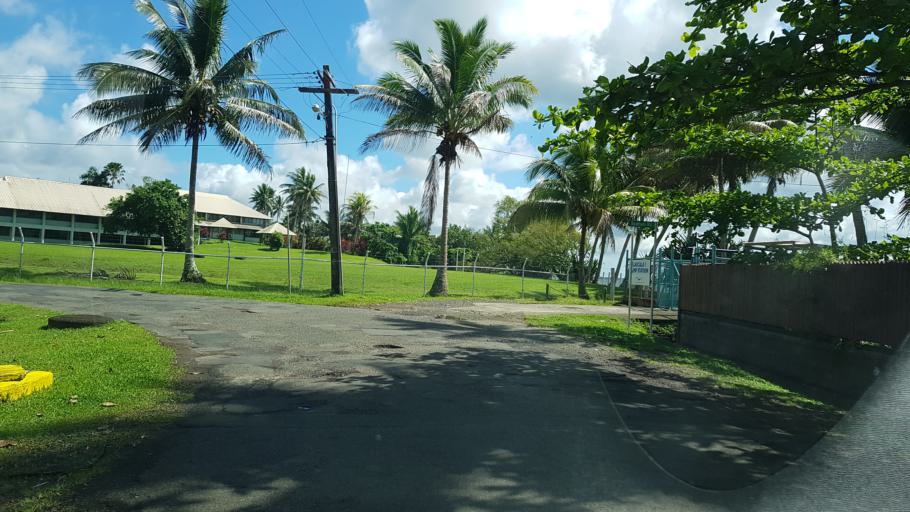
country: FJ
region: Central
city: Suva
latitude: -18.1460
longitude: 178.4564
